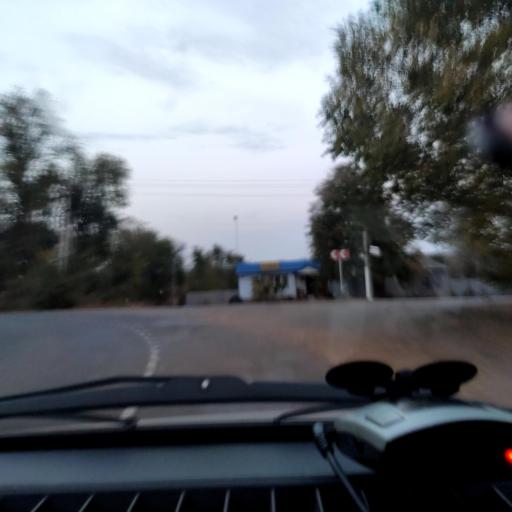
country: RU
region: Voronezj
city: Uryv-Pokrovka
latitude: 51.2283
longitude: 38.9222
